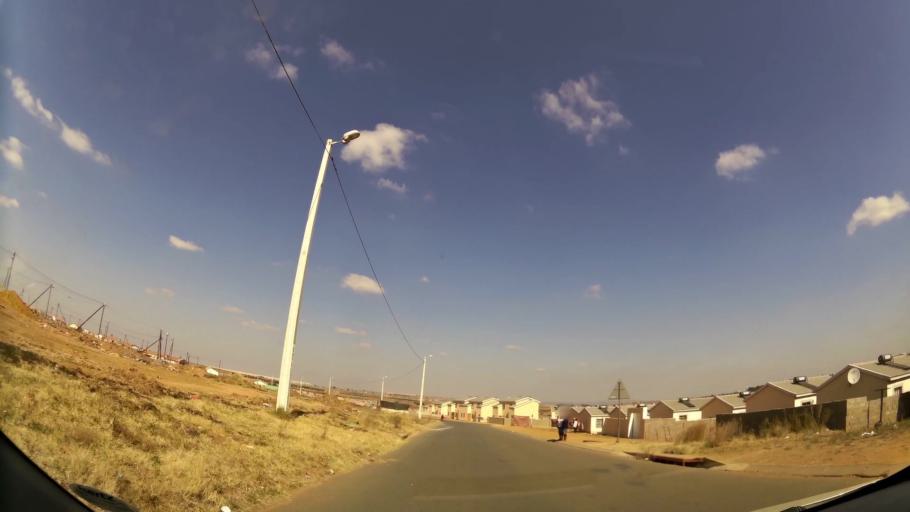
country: ZA
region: Gauteng
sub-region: West Rand District Municipality
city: Randfontein
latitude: -26.1664
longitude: 27.7704
